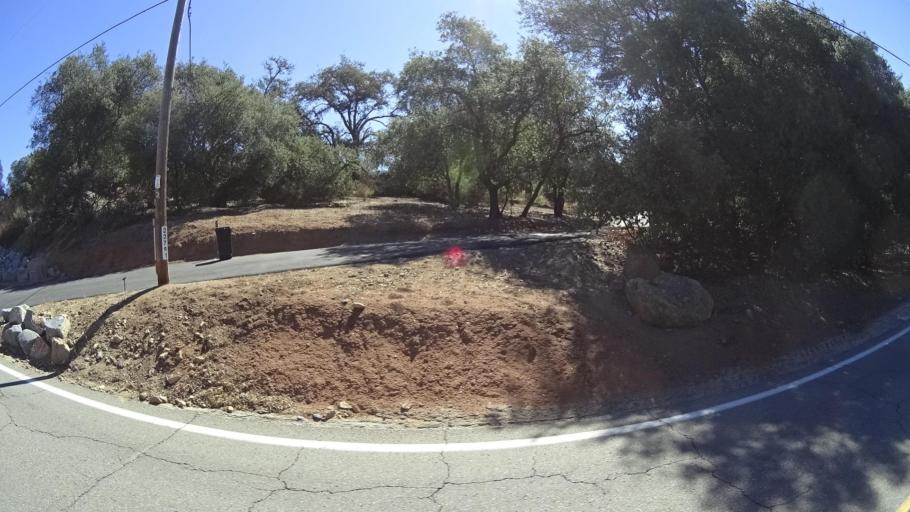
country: US
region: California
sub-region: San Diego County
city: Descanso
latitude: 32.7908
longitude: -116.6603
